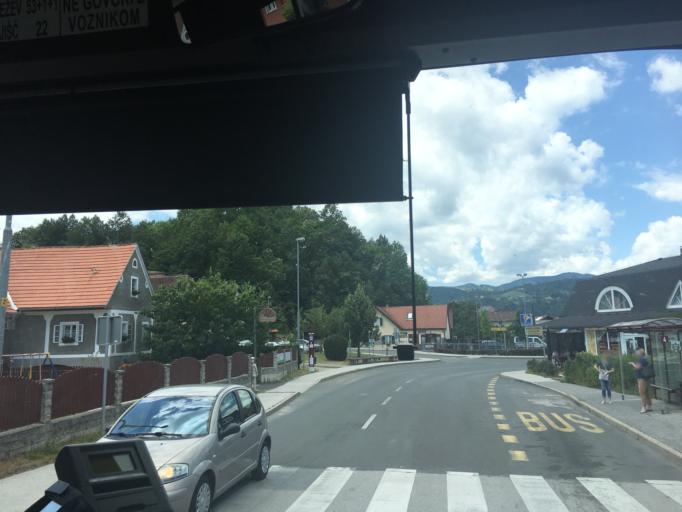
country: SI
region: Maribor
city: Limbus
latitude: 46.5537
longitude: 15.5825
